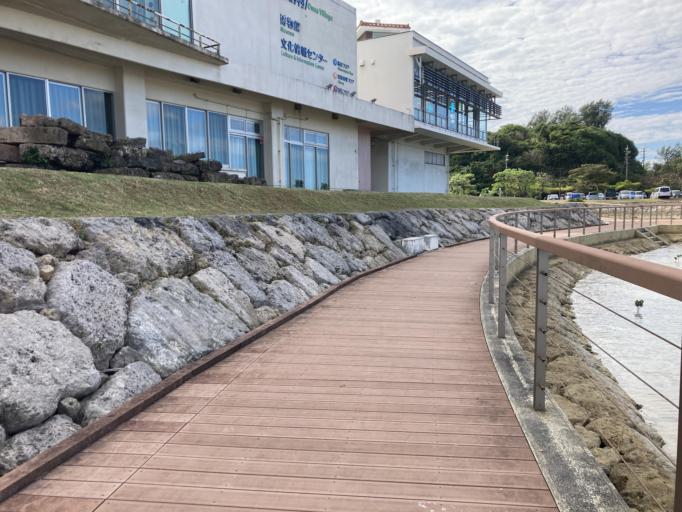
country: JP
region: Okinawa
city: Ishikawa
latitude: 26.4368
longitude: 127.7934
